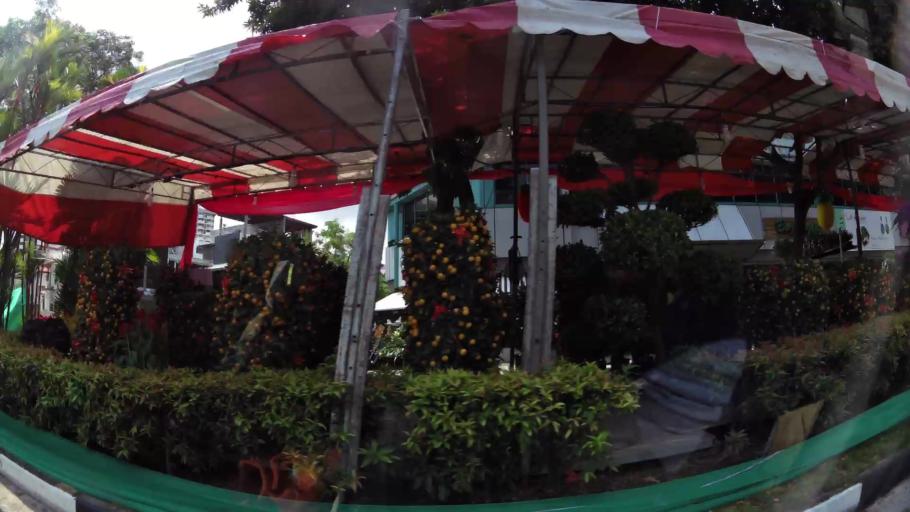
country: SG
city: Singapore
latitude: 1.3232
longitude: 103.8113
